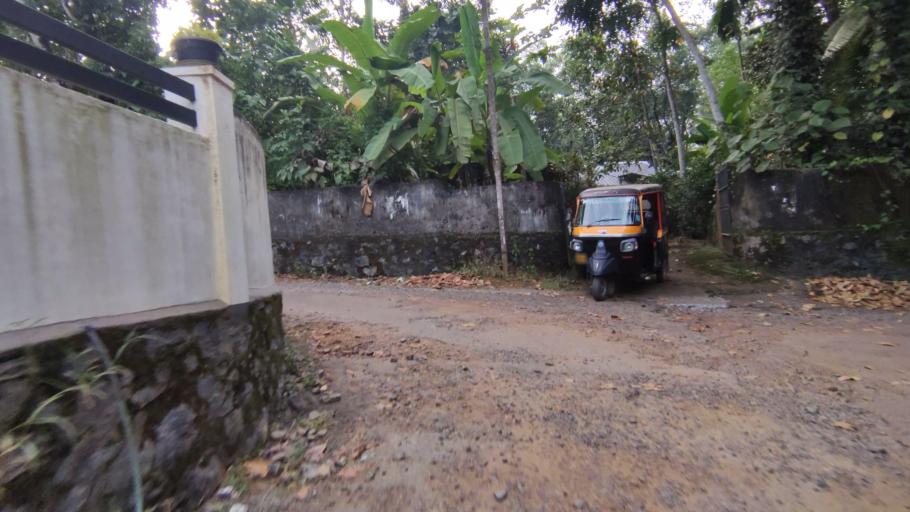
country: IN
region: Kerala
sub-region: Kottayam
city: Kottayam
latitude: 9.6366
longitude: 76.5068
